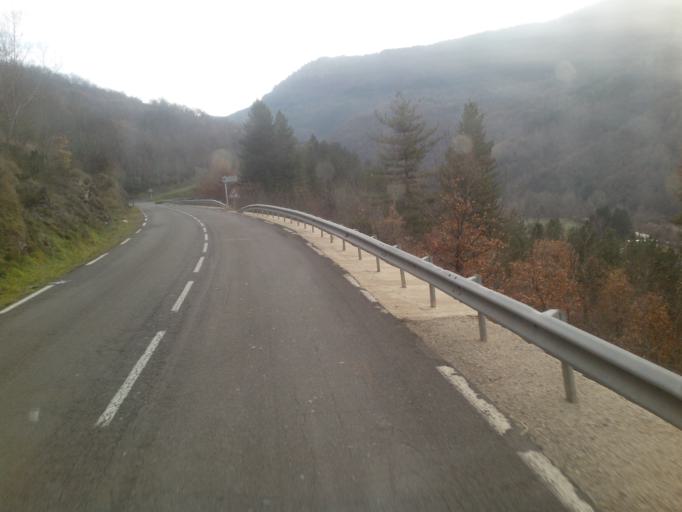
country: FR
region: Languedoc-Roussillon
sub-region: Departement de la Lozere
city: Florac
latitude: 44.3694
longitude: 3.5582
